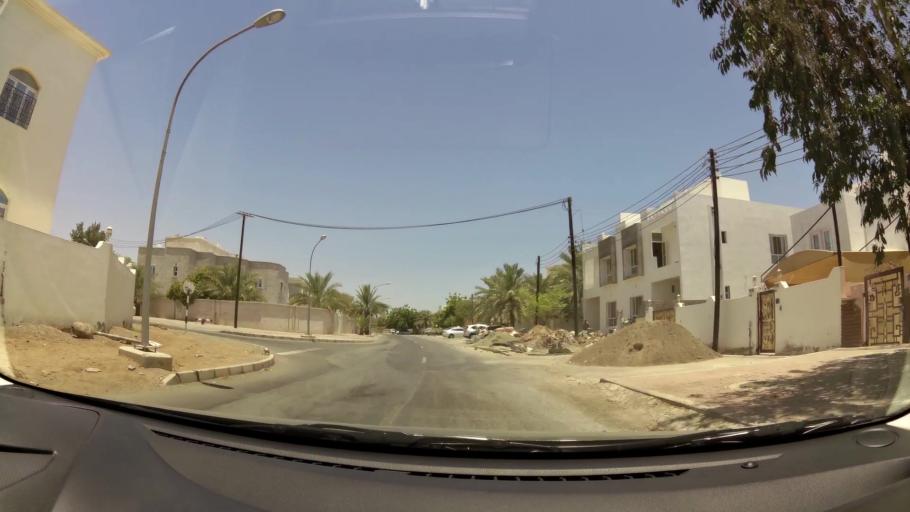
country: OM
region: Muhafazat Masqat
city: As Sib al Jadidah
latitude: 23.6349
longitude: 58.2385
